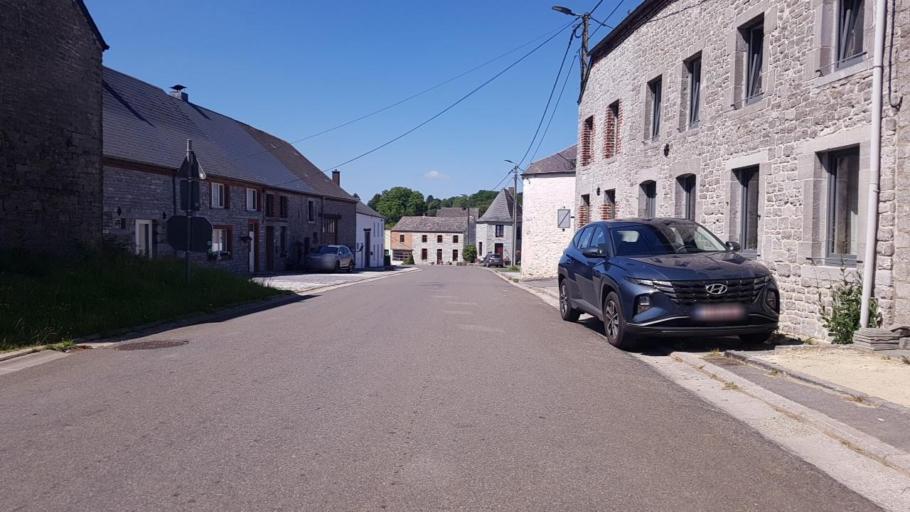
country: BE
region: Wallonia
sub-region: Province du Hainaut
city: Chimay
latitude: 50.0690
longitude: 4.2376
